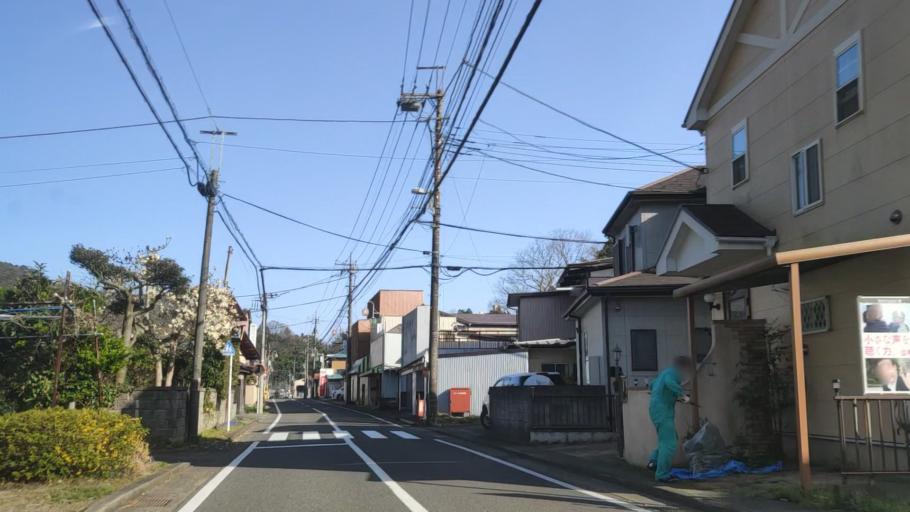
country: JP
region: Tokyo
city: Hachioji
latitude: 35.5438
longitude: 139.2686
